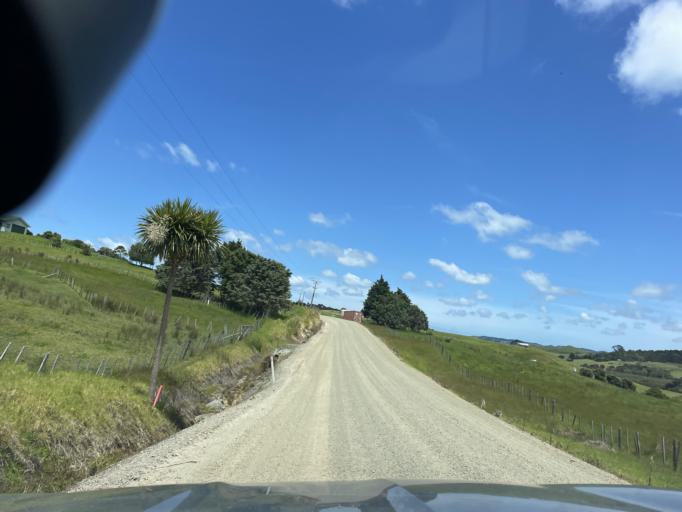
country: NZ
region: Auckland
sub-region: Auckland
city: Wellsford
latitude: -36.1704
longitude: 174.2755
